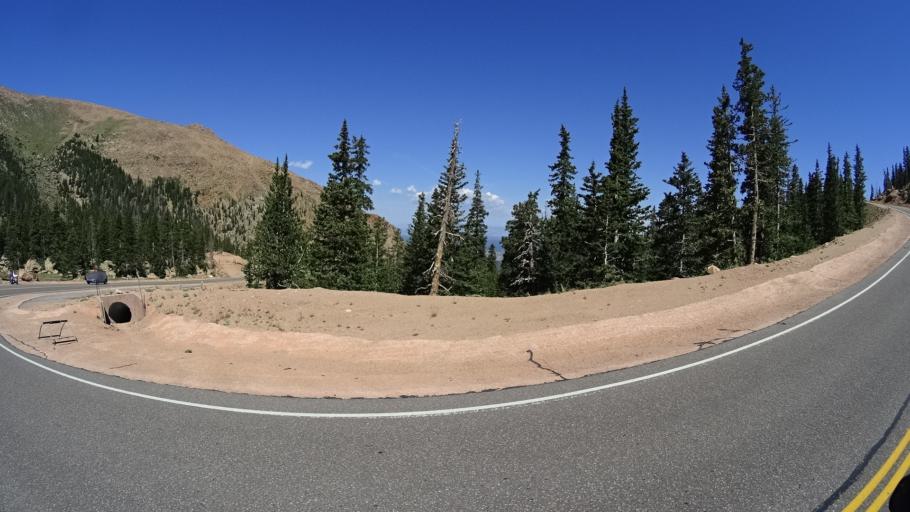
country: US
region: Colorado
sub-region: El Paso County
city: Cascade-Chipita Park
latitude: 38.8723
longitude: -105.0704
